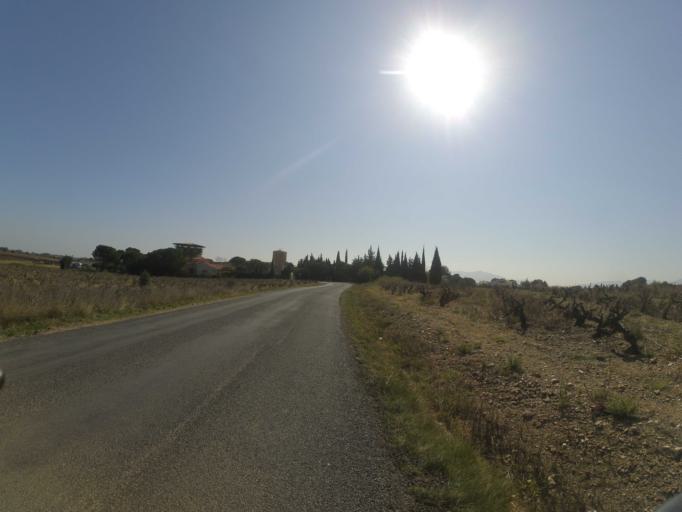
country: FR
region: Languedoc-Roussillon
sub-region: Departement des Pyrenees-Orientales
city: Llupia
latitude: 42.6098
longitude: 2.7670
